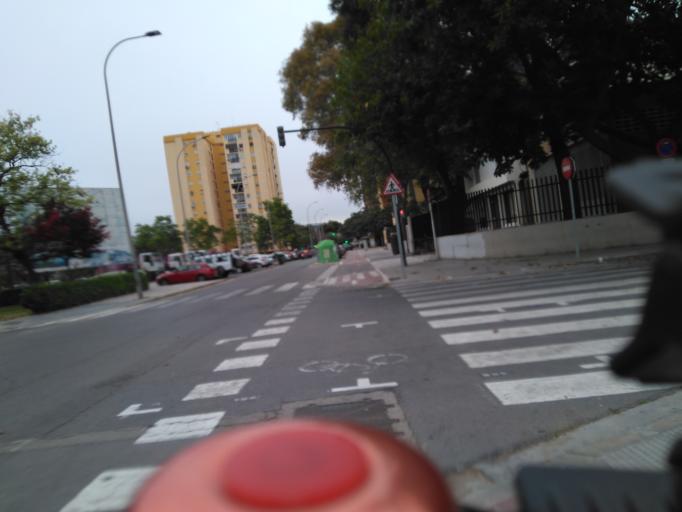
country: ES
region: Valencia
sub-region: Provincia de Valencia
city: Mislata
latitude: 39.4668
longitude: -0.4034
